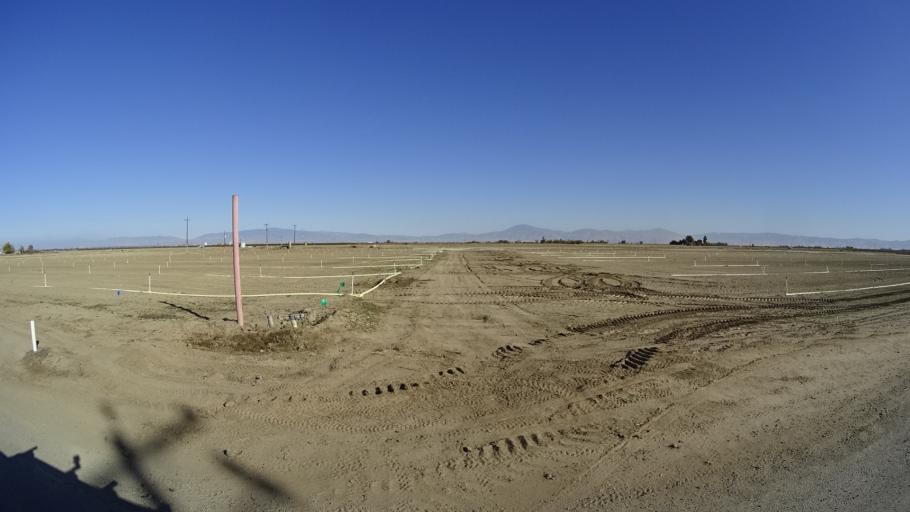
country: US
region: California
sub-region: Kern County
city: Greenfield
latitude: 35.2728
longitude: -119.1099
